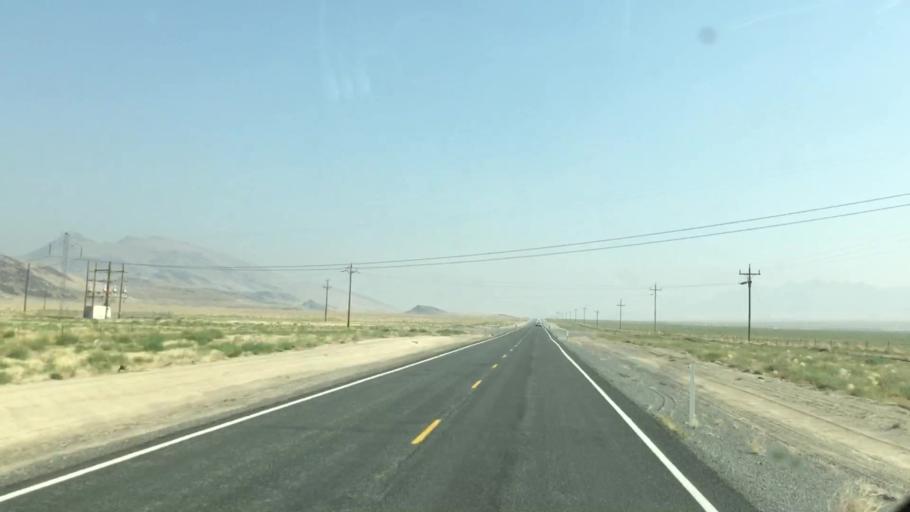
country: US
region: Nevada
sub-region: Lyon County
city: Fernley
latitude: 40.3461
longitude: -119.3396
